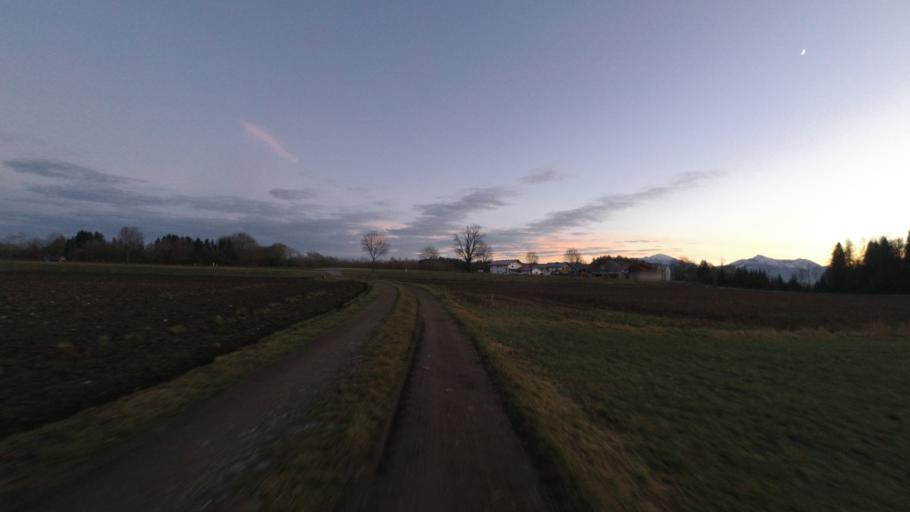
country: DE
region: Bavaria
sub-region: Upper Bavaria
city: Chieming
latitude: 47.9090
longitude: 12.5549
